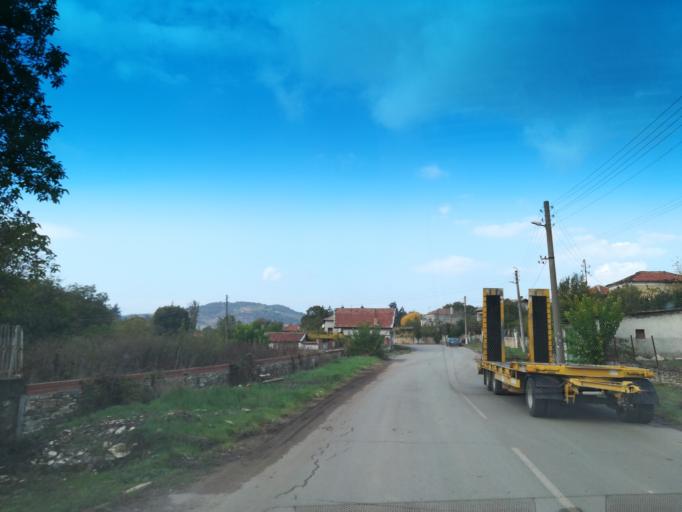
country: BG
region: Stara Zagora
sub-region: Obshtina Nikolaevo
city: Elkhovo
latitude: 42.3406
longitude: 25.4025
